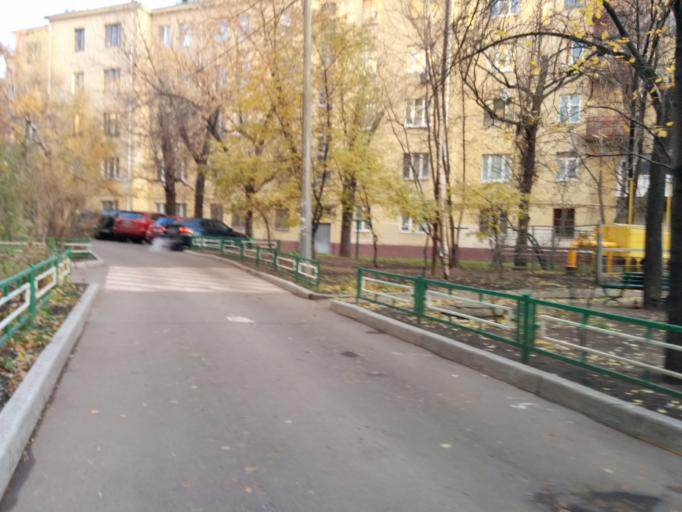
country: RU
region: Moscow
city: Novyye Cheremushki
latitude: 55.7120
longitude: 37.6101
